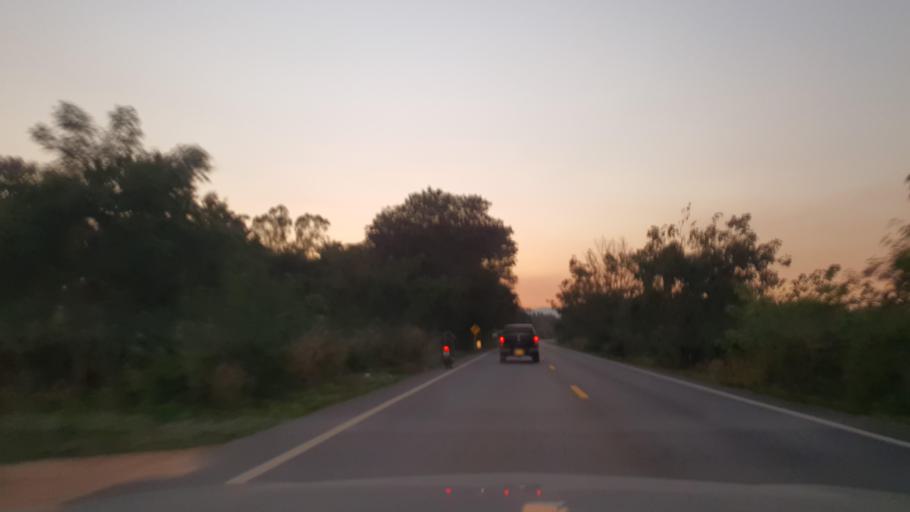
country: TH
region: Phayao
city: Dok Kham Tai
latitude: 19.1482
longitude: 100.0109
